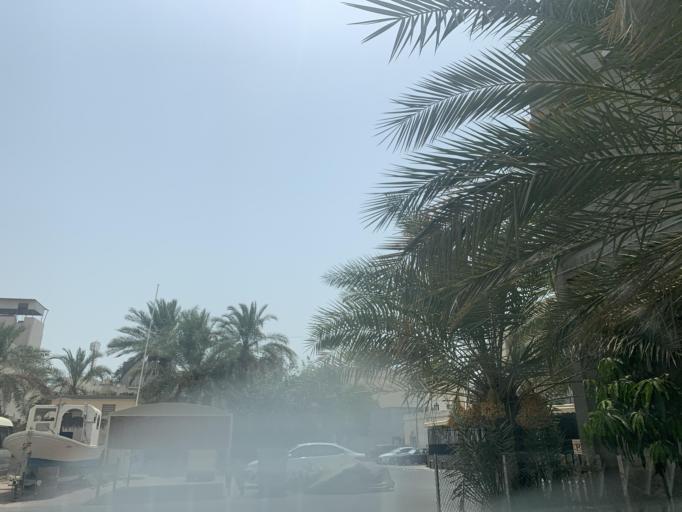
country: BH
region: Manama
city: Jidd Hafs
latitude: 26.1980
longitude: 50.4662
